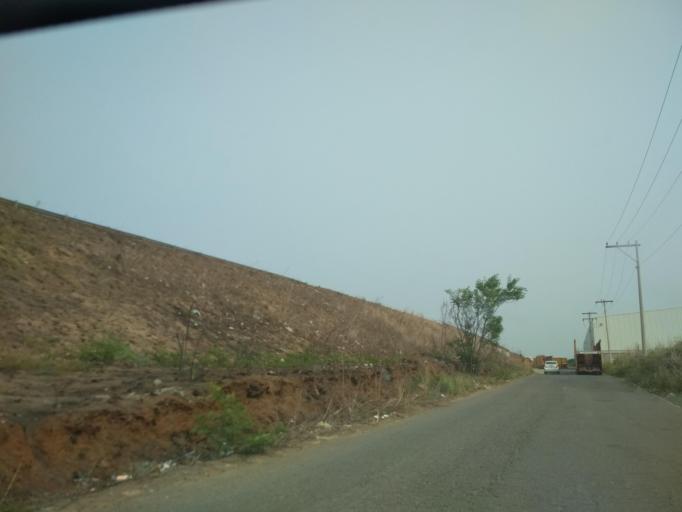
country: MX
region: Veracruz
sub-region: Veracruz
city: Delfino Victoria (Santa Fe)
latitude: 19.1660
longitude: -96.2656
